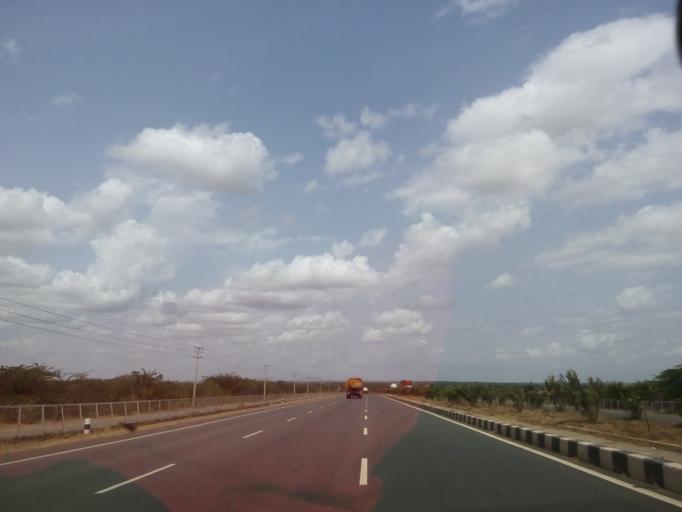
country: IN
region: Karnataka
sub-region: Chitradurga
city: Hiriyur
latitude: 13.8525
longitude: 76.7213
